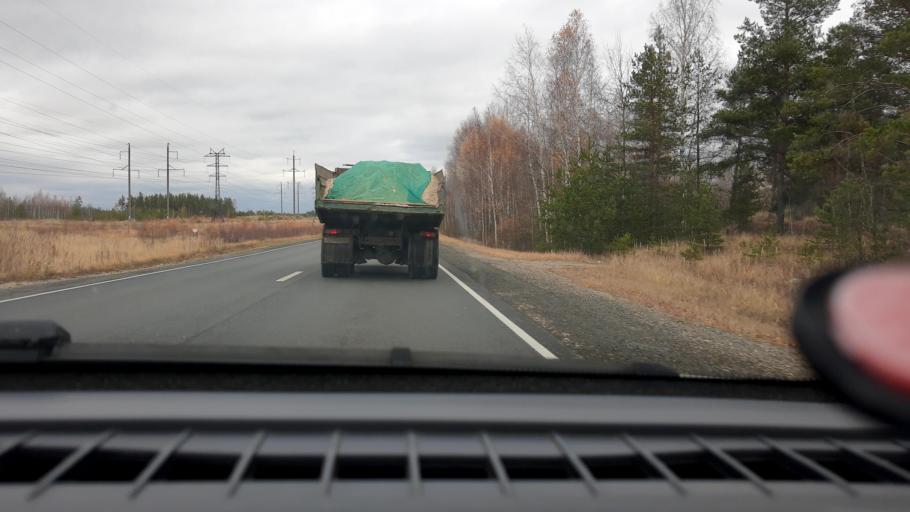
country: RU
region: Nizjnij Novgorod
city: Lukino
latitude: 56.3753
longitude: 43.6249
